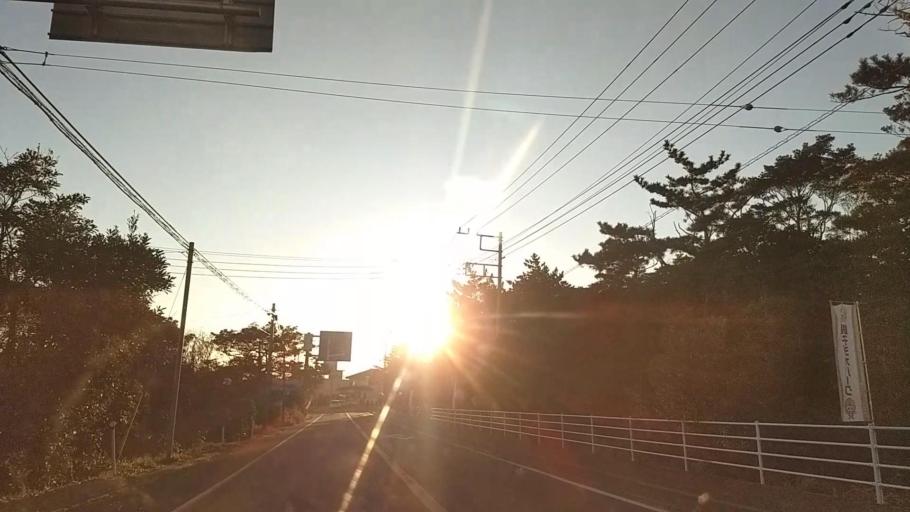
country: JP
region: Chiba
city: Hasaki
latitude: 35.7066
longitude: 140.8634
